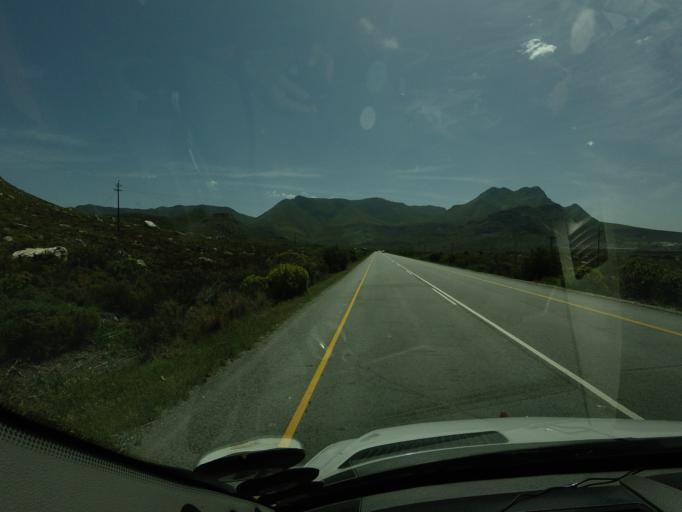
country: ZA
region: Western Cape
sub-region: Overberg District Municipality
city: Grabouw
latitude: -34.3418
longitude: 18.9830
